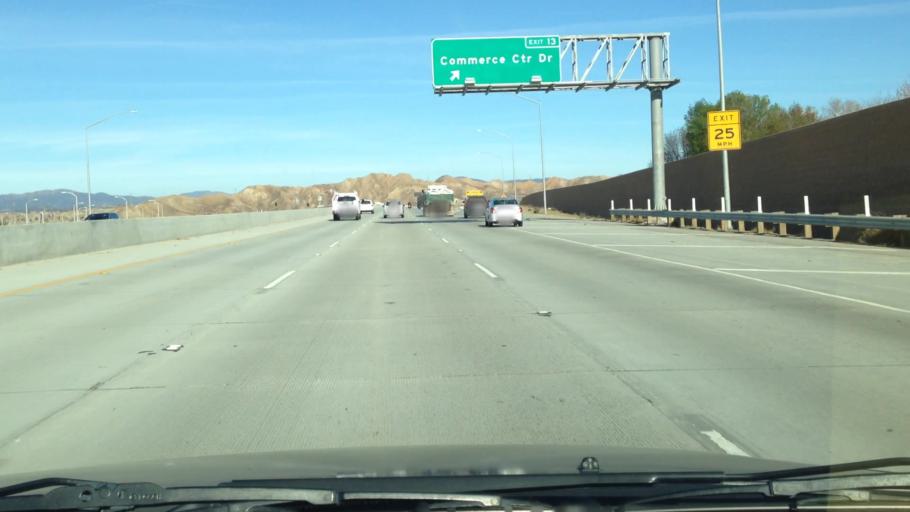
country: US
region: California
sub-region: Los Angeles County
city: Valencia
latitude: 34.4310
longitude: -118.6230
